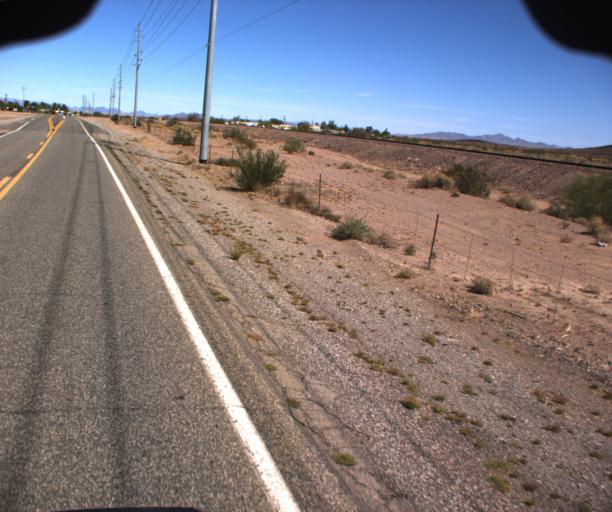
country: US
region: Arizona
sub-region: La Paz County
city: Cienega Springs
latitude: 33.9255
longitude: -114.0003
